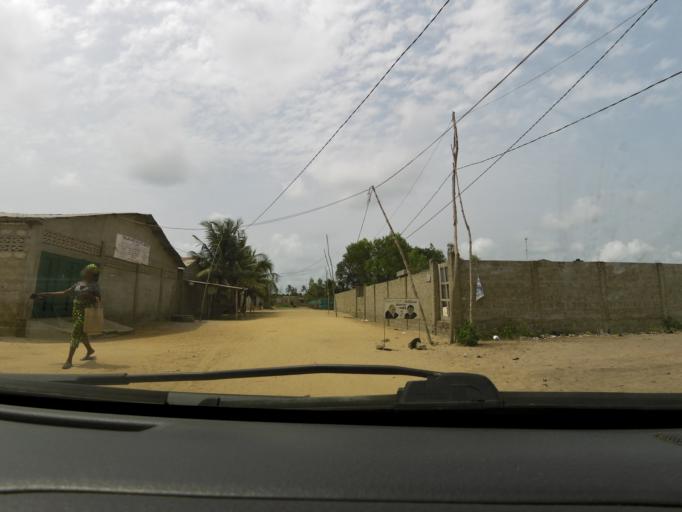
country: BJ
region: Queme
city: Porto-Novo
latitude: 6.3751
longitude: 2.6267
